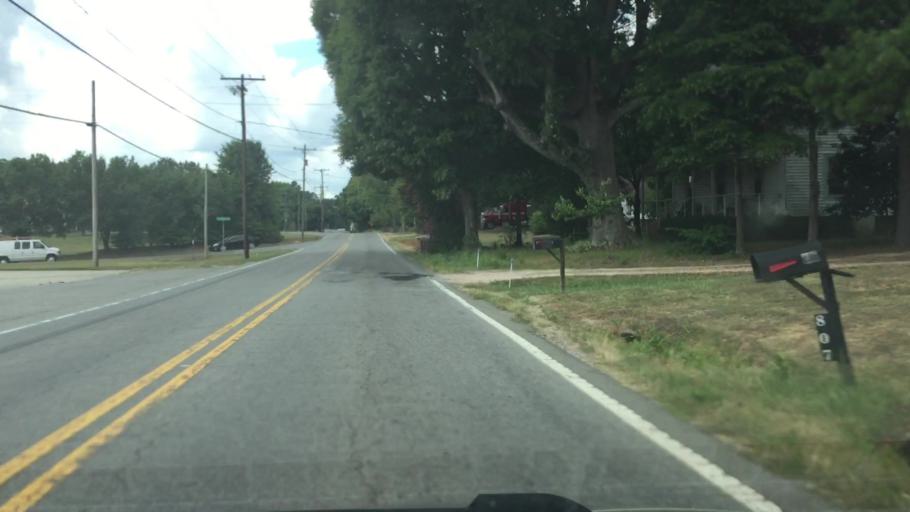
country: US
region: North Carolina
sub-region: Rowan County
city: Enochville
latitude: 35.5308
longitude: -80.6671
